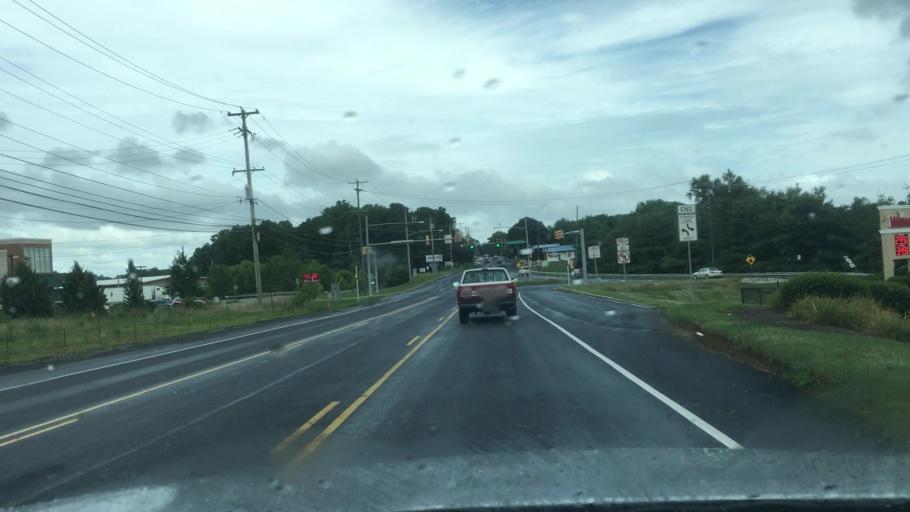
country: US
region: Pennsylvania
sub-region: Chester County
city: Avondale
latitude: 39.8348
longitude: -75.7946
